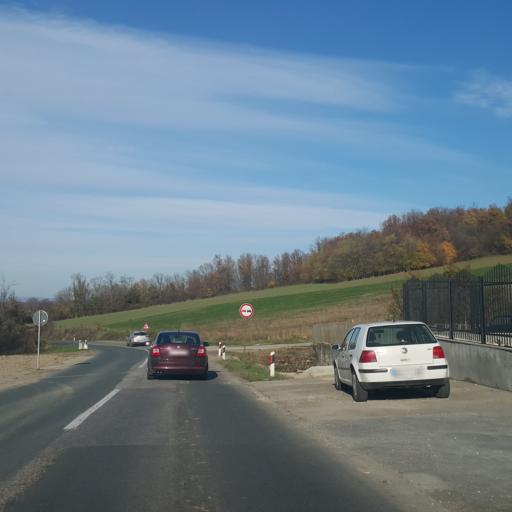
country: RS
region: Central Serbia
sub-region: Sumadijski Okrug
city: Topola
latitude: 44.2715
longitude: 20.6935
